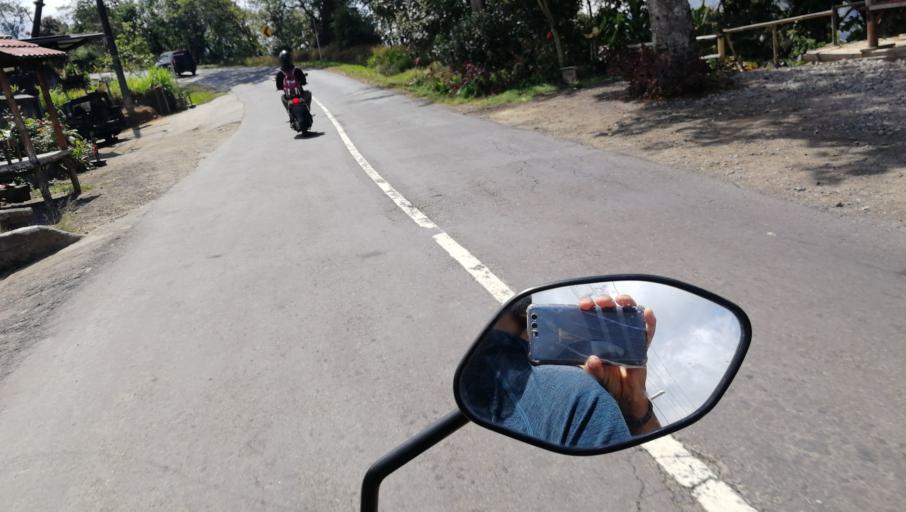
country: ID
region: Bali
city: Munduk
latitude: -8.2368
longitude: 115.1282
